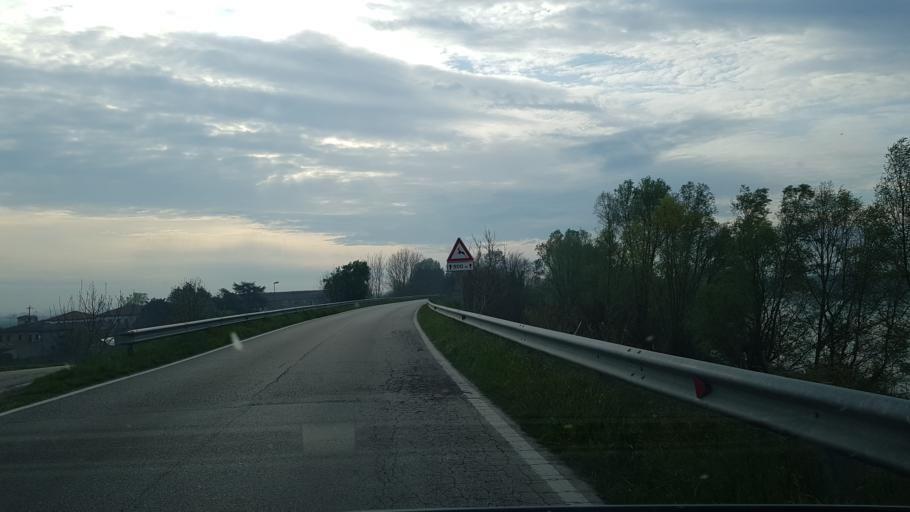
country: IT
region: Veneto
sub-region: Provincia di Rovigo
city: Lendinara
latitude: 45.1187
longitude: 11.5995
